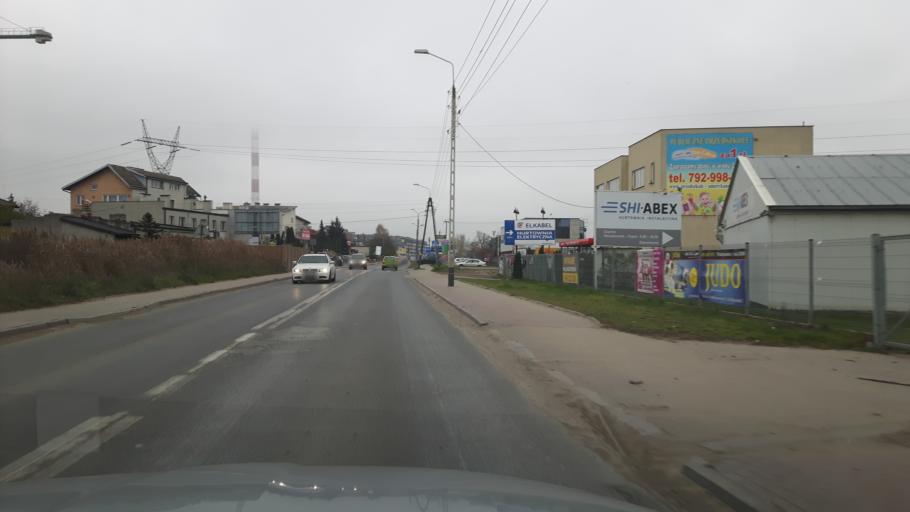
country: PL
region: Masovian Voivodeship
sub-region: Powiat wolominski
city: Zabki
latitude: 52.2802
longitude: 21.1131
